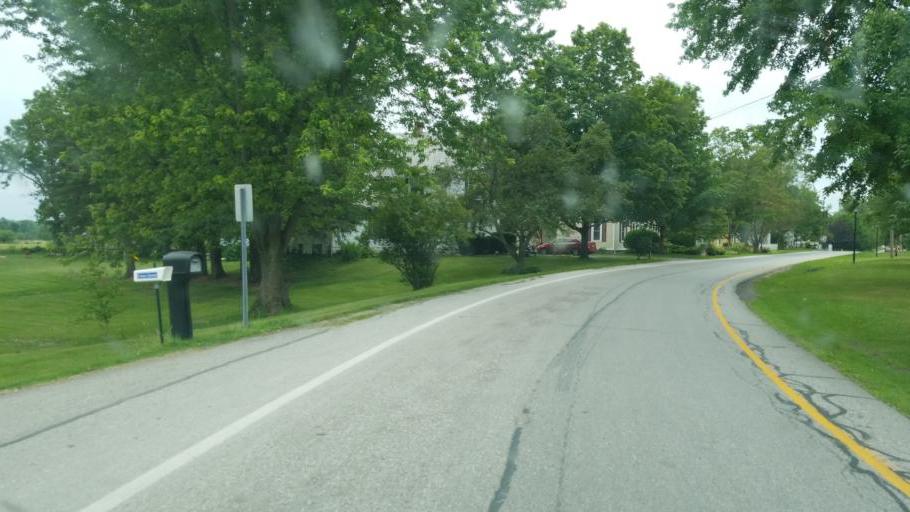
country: US
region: Ohio
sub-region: Ashtabula County
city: Orwell
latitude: 41.4630
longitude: -80.9543
